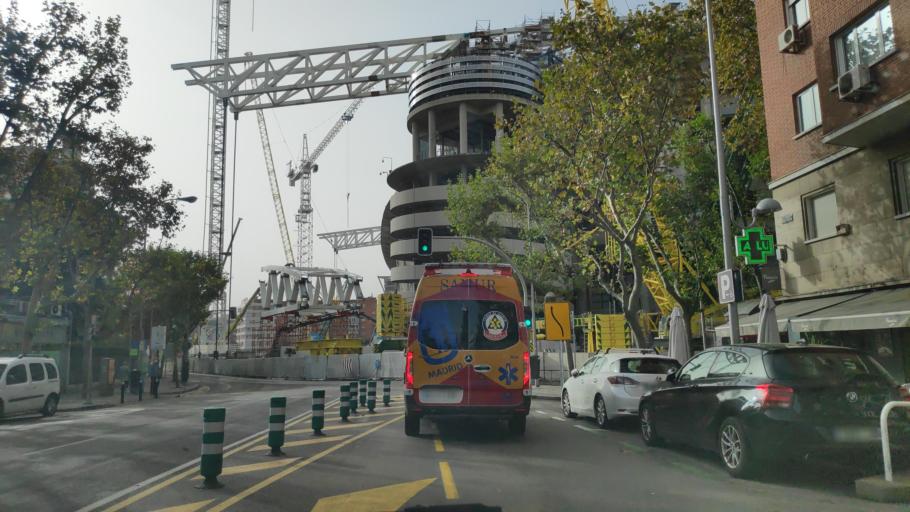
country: ES
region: Madrid
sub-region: Provincia de Madrid
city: Chamartin
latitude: 40.4546
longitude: -3.6872
